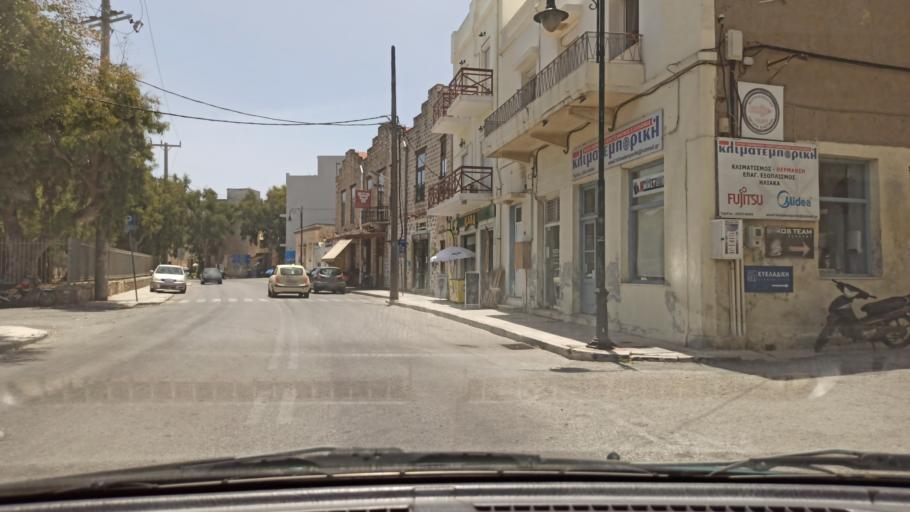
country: GR
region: South Aegean
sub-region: Nomos Kykladon
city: Ermoupolis
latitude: 37.4327
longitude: 24.9349
